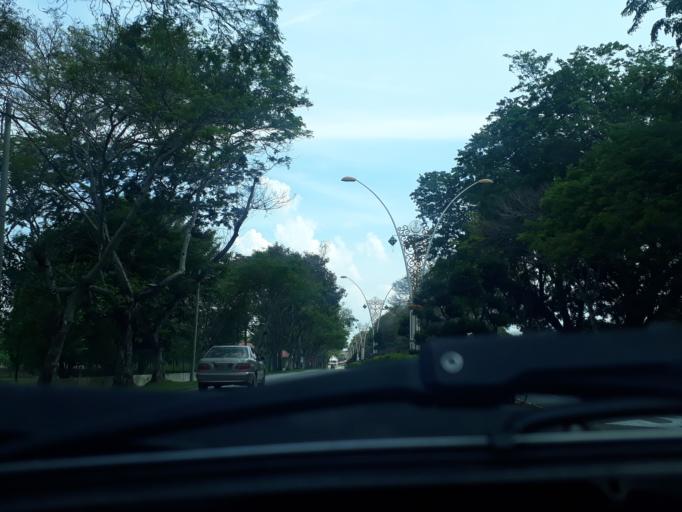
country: MY
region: Perak
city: Ipoh
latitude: 4.5842
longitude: 101.1094
